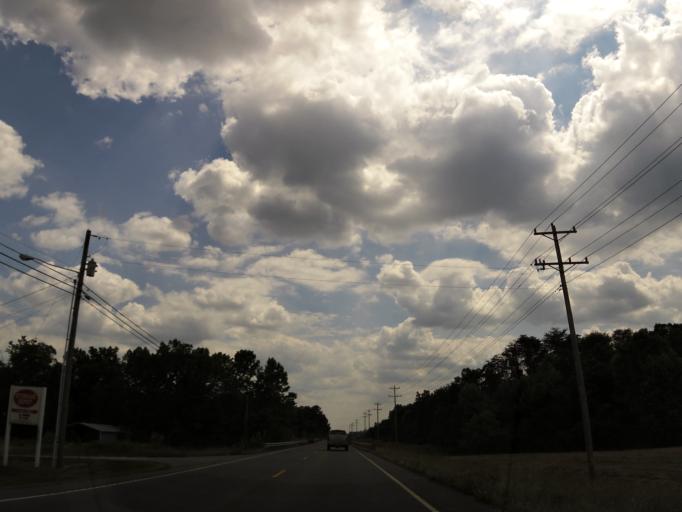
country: US
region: Tennessee
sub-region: Sequatchie County
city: Dunlap
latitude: 35.4094
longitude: -85.3666
